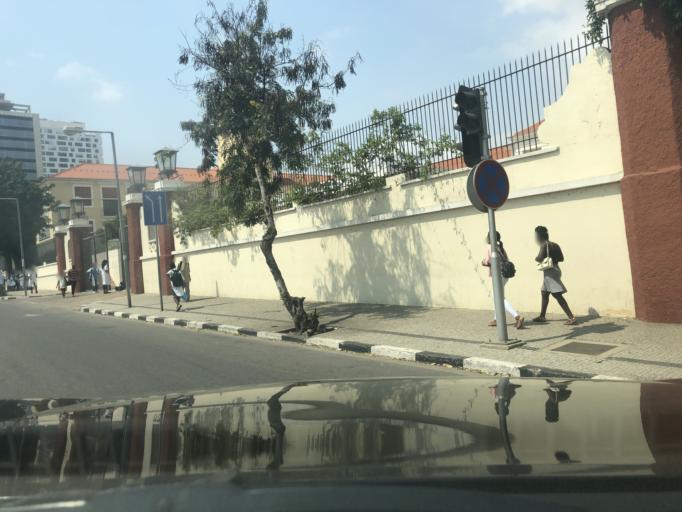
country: AO
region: Luanda
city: Luanda
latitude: -8.8218
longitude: 13.2333
